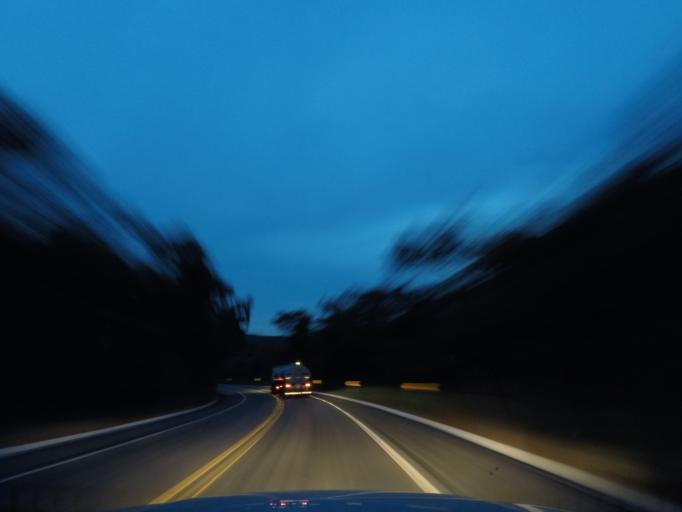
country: BR
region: Bahia
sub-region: Andarai
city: Vera Cruz
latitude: -12.4914
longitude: -41.3271
